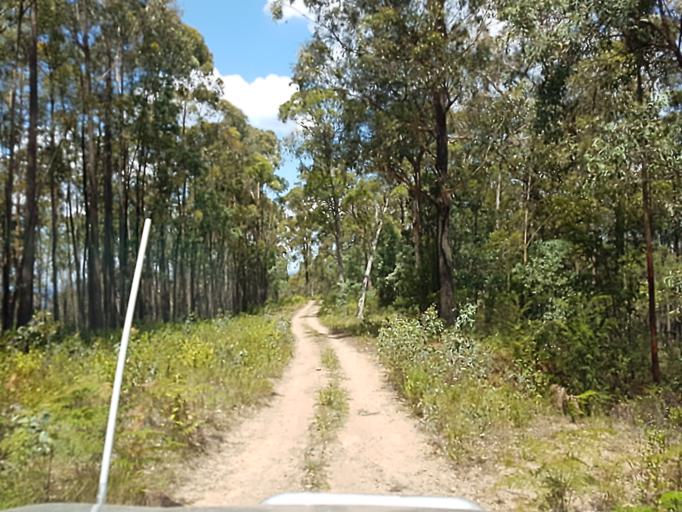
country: AU
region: Victoria
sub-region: East Gippsland
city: Lakes Entrance
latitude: -37.4048
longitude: 148.3006
